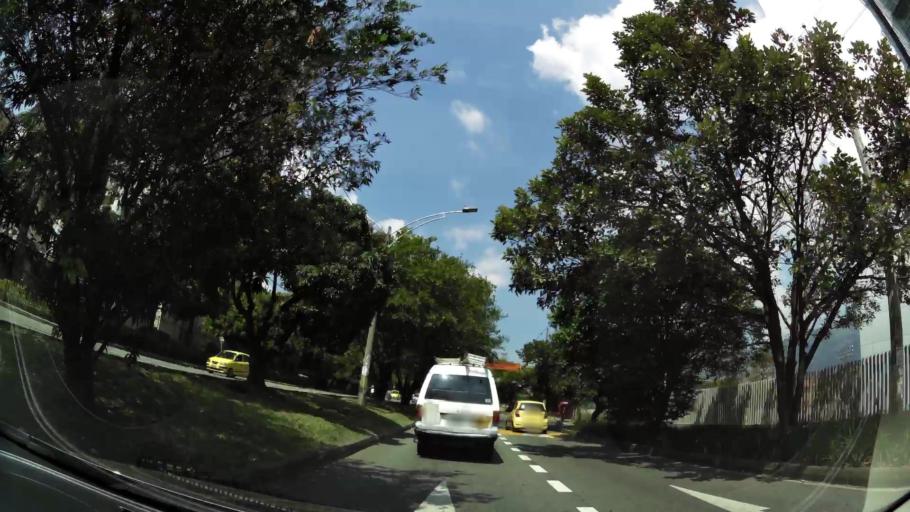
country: CO
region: Antioquia
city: Medellin
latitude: 6.2784
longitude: -75.5804
